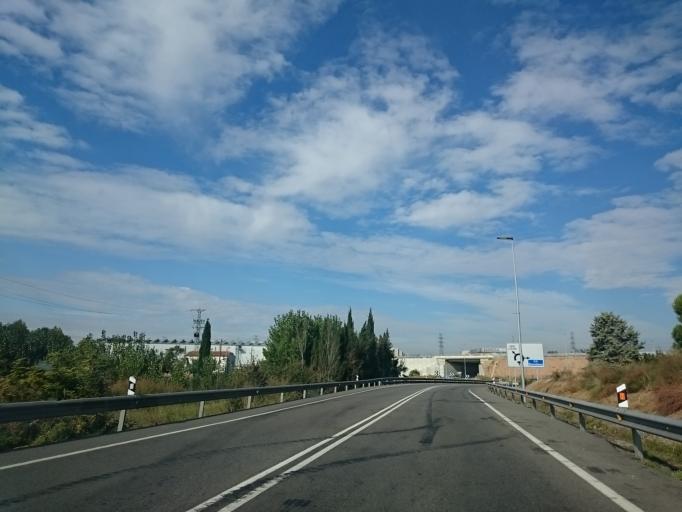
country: ES
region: Catalonia
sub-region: Provincia de Lleida
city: Alcoletge
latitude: 41.6045
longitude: 0.6808
